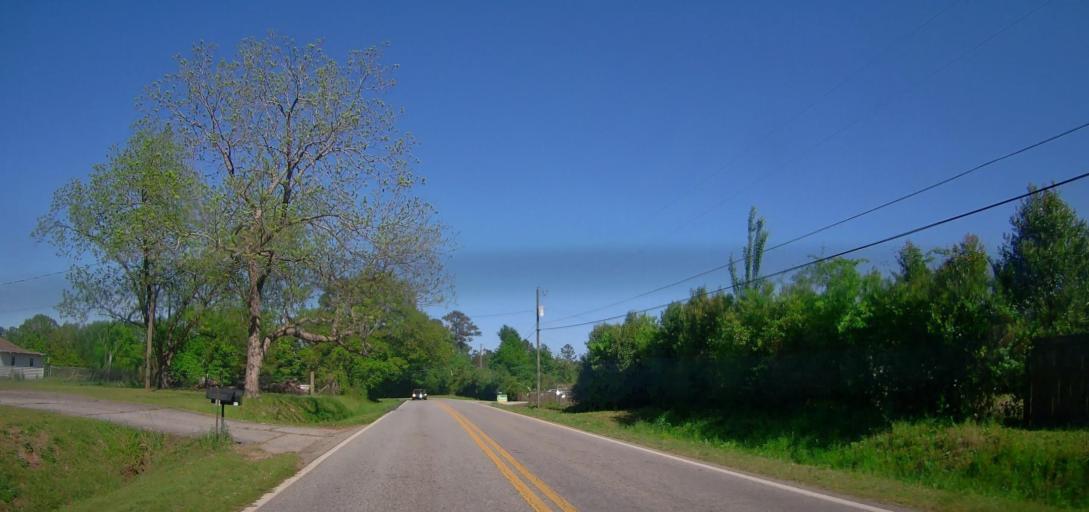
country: US
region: Georgia
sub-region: Houston County
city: Warner Robins
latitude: 32.6561
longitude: -83.6332
